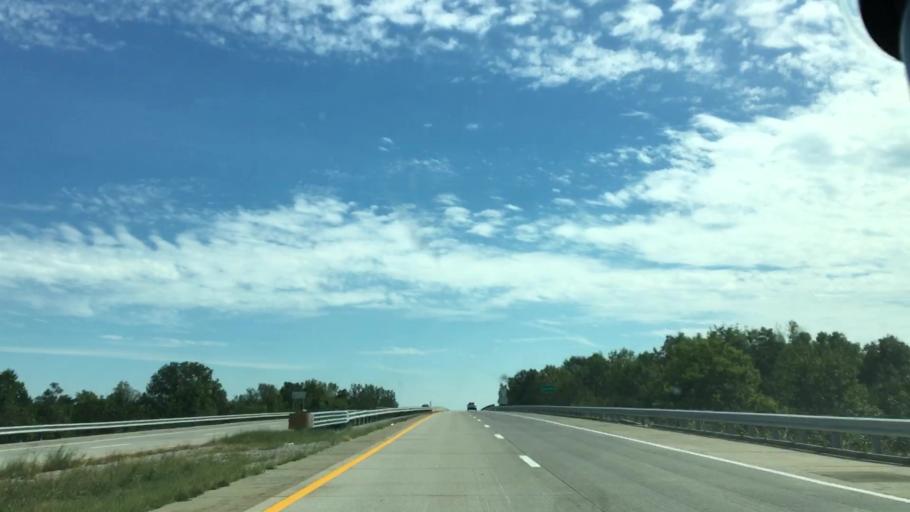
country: US
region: Kentucky
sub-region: Daviess County
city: Owensboro
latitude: 37.7583
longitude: -87.2991
